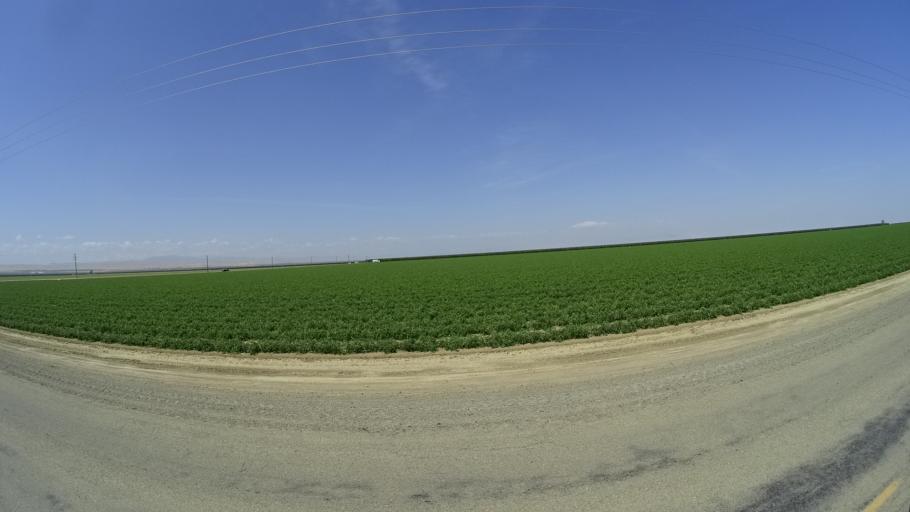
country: US
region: California
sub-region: Kings County
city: Kettleman City
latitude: 36.1246
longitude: -120.0037
